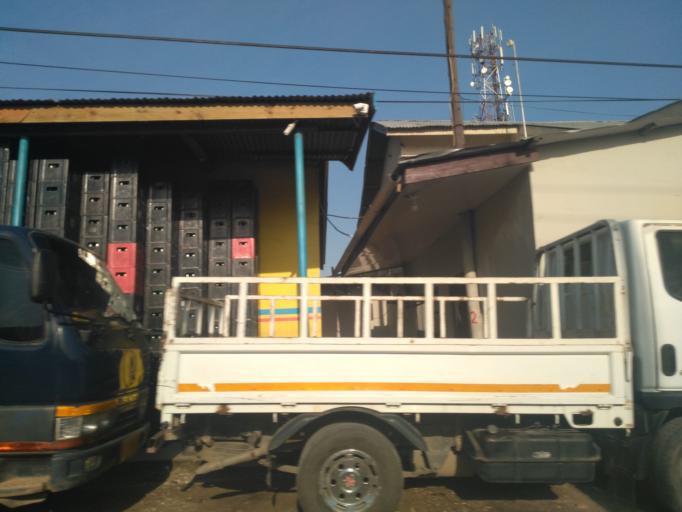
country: TZ
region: Dar es Salaam
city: Magomeni
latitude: -6.7878
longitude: 39.2653
